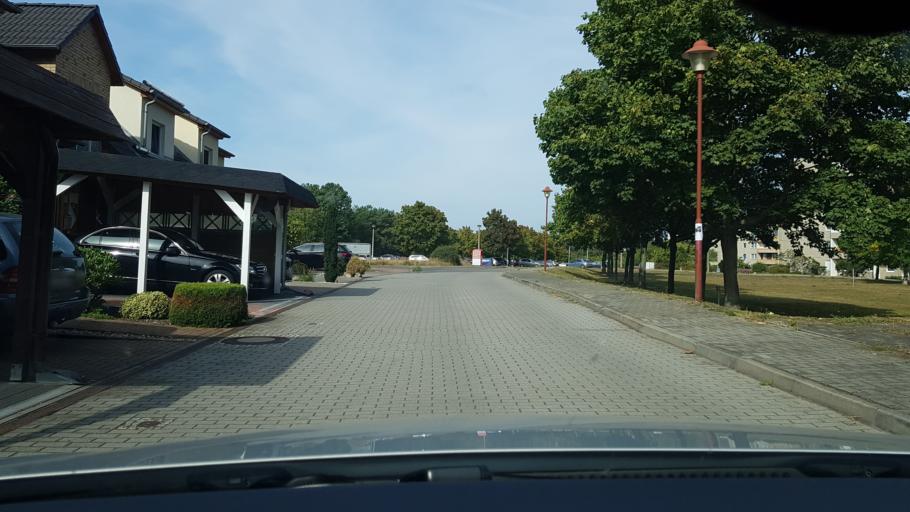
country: DE
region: Brandenburg
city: Lawitz
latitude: 52.1285
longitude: 14.6410
